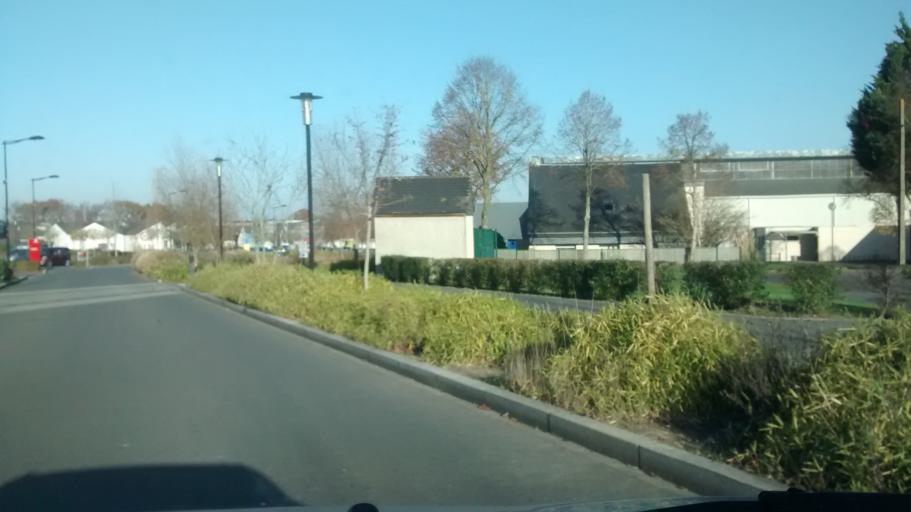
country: FR
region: Brittany
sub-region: Departement d'Ille-et-Vilaine
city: Pace
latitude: 48.1521
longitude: -1.7705
